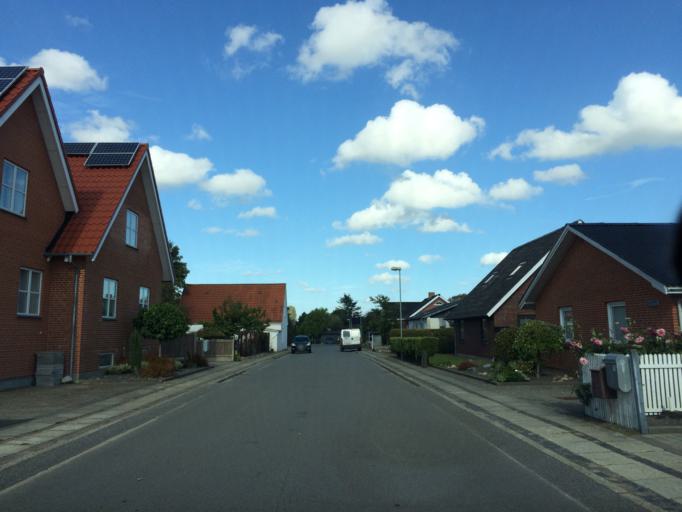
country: DK
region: Central Jutland
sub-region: Holstebro Kommune
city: Ulfborg
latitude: 56.2695
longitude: 8.3226
